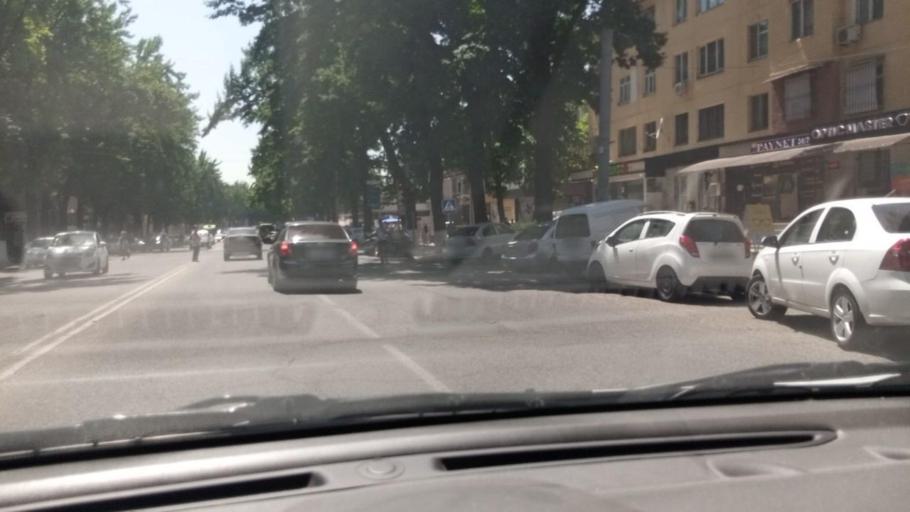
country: UZ
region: Toshkent Shahri
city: Tashkent
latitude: 41.2847
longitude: 69.2255
